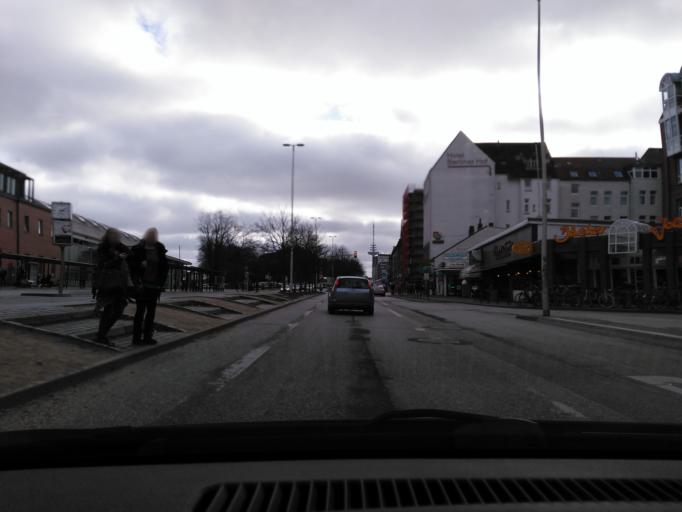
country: DE
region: Schleswig-Holstein
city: Kiel
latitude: 54.3156
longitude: 10.1312
